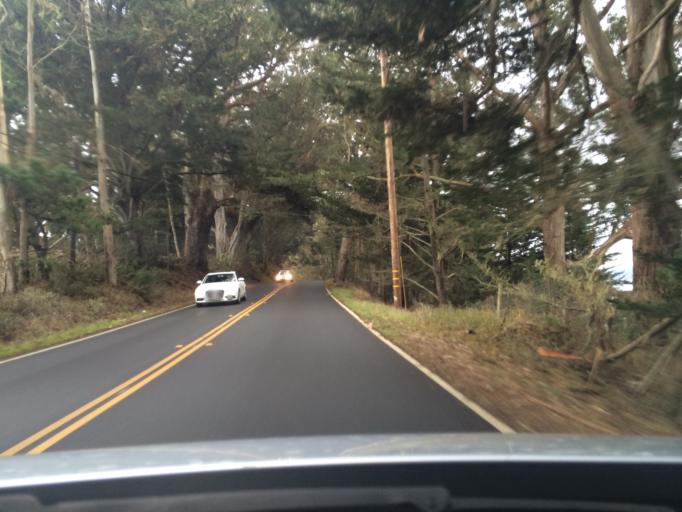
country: US
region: California
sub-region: Marin County
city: Inverness
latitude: 38.1897
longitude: -122.9144
